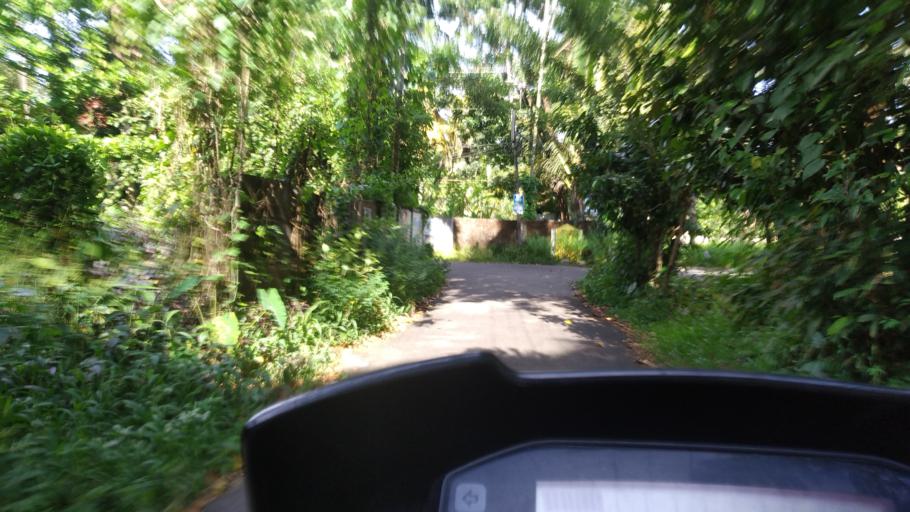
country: IN
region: Kerala
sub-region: Ernakulam
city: Elur
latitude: 10.0724
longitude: 76.2146
